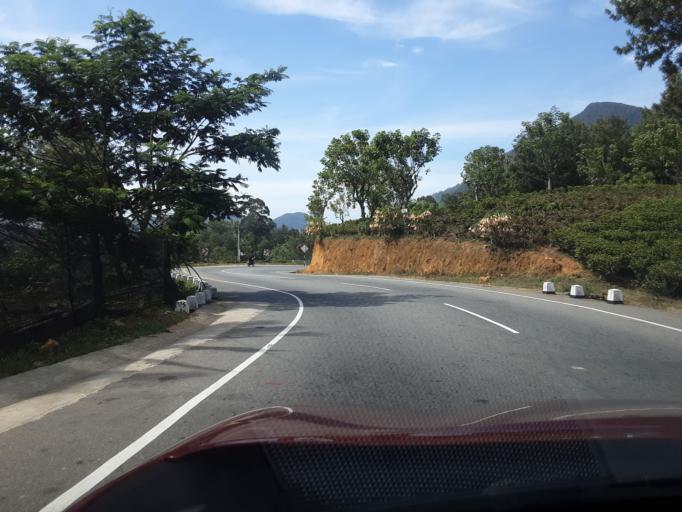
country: LK
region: Uva
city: Badulla
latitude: 6.9544
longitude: 81.1220
